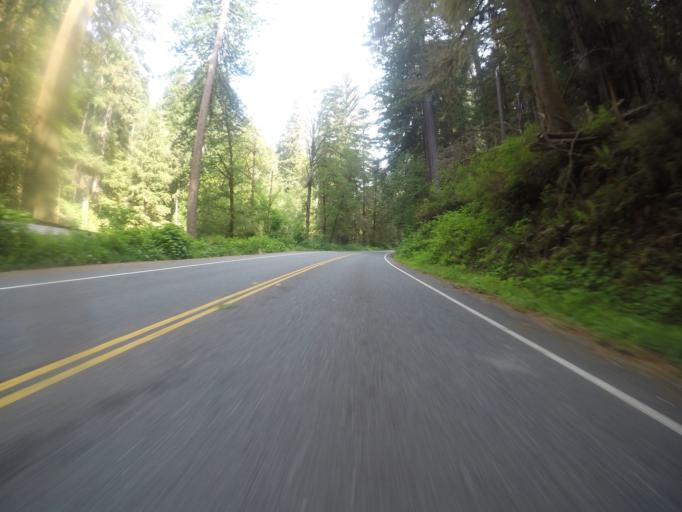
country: US
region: California
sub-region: Del Norte County
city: Bertsch-Oceanview
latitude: 41.4234
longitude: -124.0359
